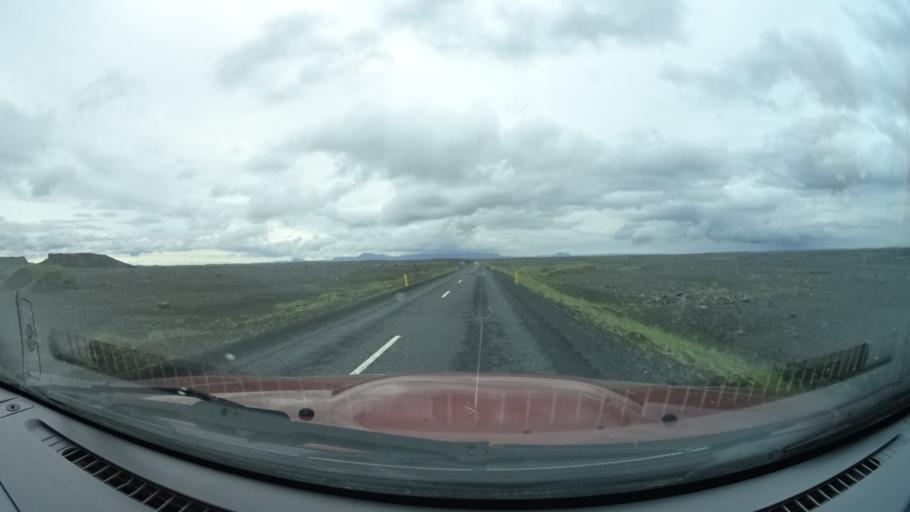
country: IS
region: Northeast
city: Laugar
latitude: 65.6211
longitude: -16.2352
